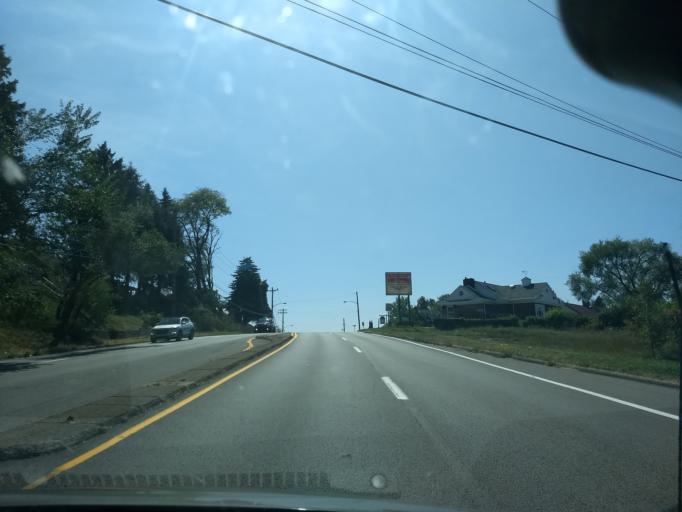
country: US
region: Pennsylvania
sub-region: Allegheny County
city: North Versailles
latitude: 40.3787
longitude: -79.8282
